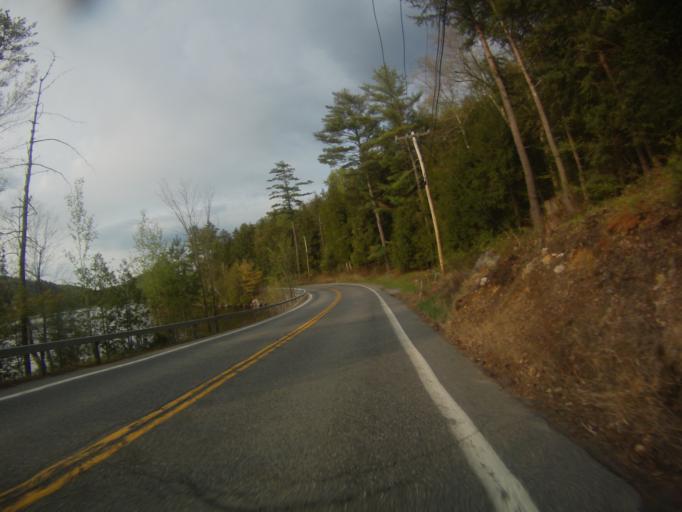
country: US
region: New York
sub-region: Warren County
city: Warrensburg
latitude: 43.7013
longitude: -73.7130
